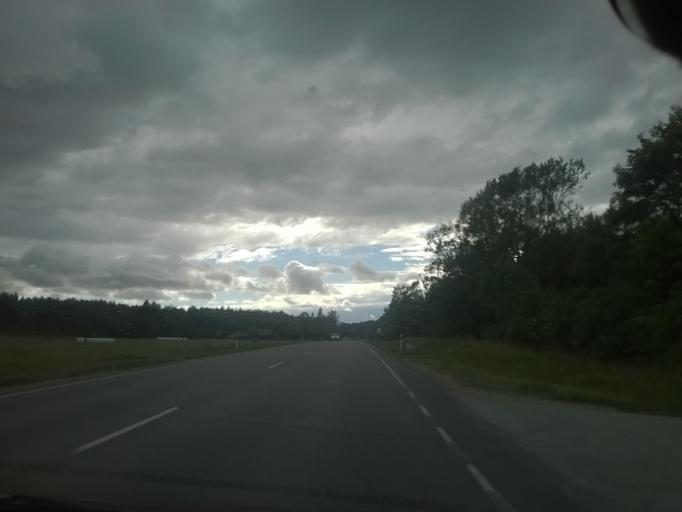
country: EE
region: Laeaene
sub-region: Ridala Parish
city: Uuemoisa
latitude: 58.9599
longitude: 23.7089
